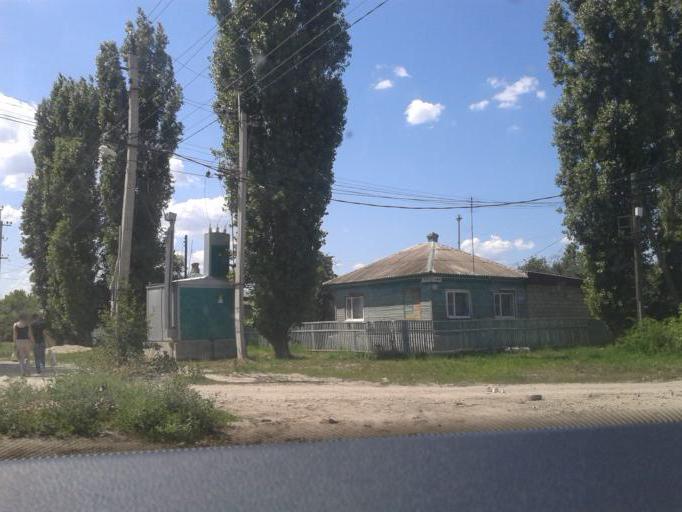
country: RU
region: Volgograd
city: Frolovo
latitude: 49.7602
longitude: 43.6623
